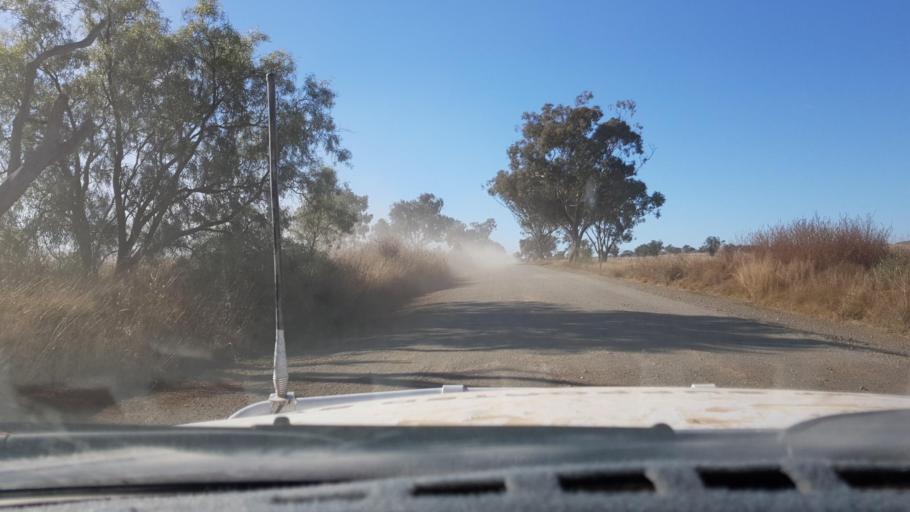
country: AU
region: New South Wales
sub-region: Narrabri
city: Blair Athol
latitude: -30.6680
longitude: 150.3704
